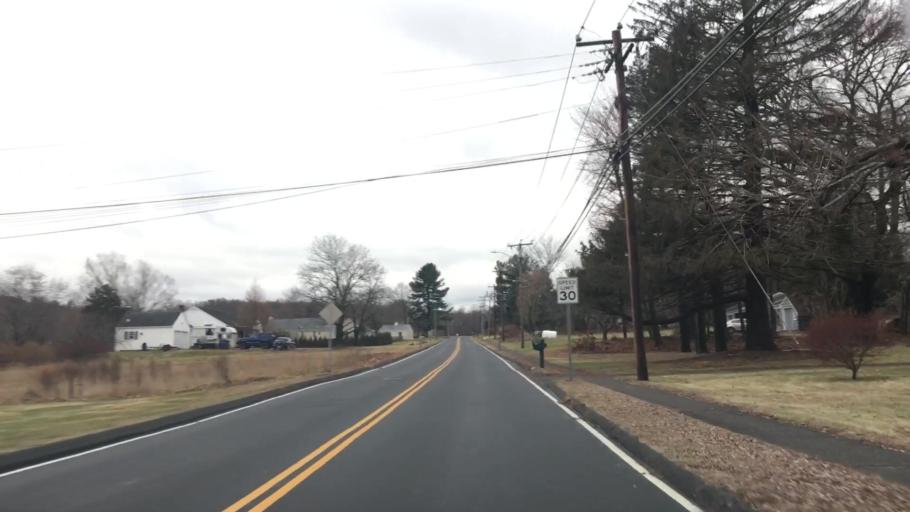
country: US
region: Connecticut
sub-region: Tolland County
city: Rockville
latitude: 41.8510
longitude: -72.4942
